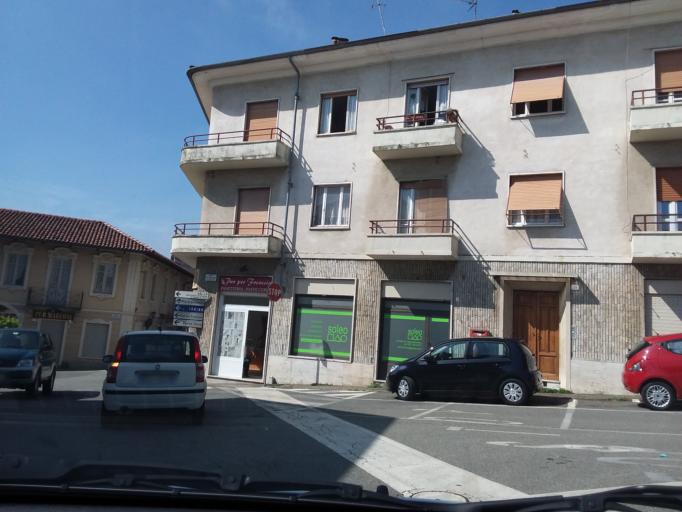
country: IT
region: Piedmont
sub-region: Provincia di Torino
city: Rivoli
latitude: 45.0681
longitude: 7.5113
